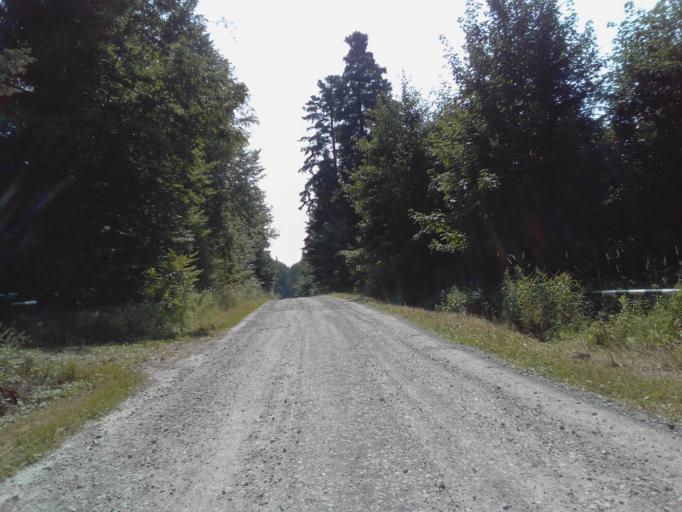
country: PL
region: Subcarpathian Voivodeship
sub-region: Powiat strzyzowski
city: Czudec
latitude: 49.9579
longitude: 21.7947
